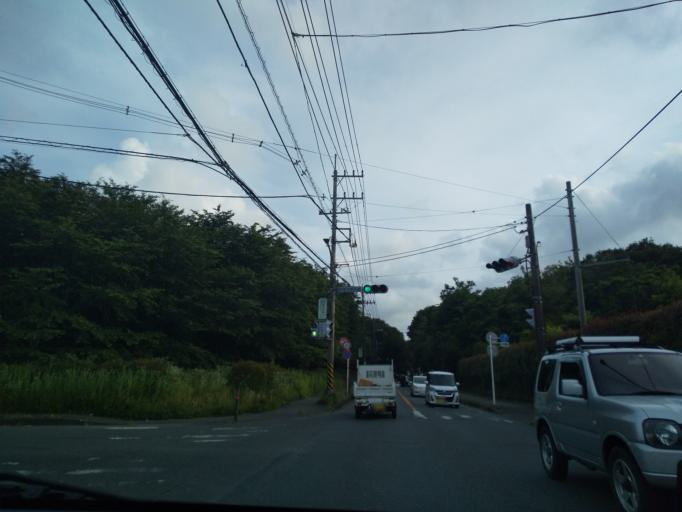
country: JP
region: Kanagawa
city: Zama
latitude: 35.5171
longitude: 139.3934
